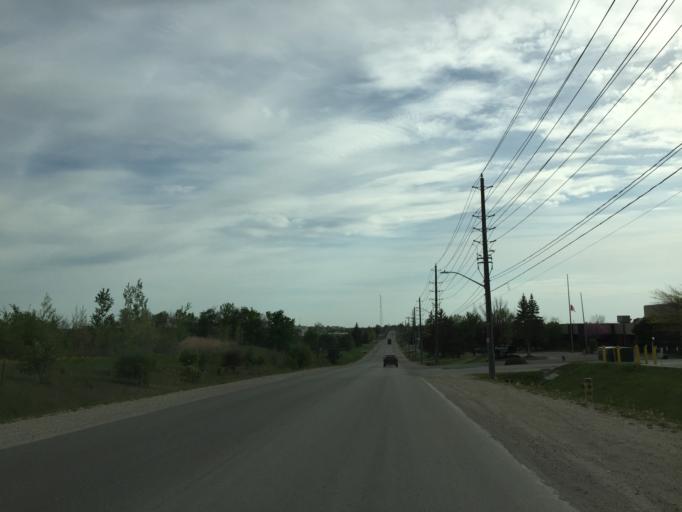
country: CA
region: Ontario
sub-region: Wellington County
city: Guelph
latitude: 43.5387
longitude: -80.3047
